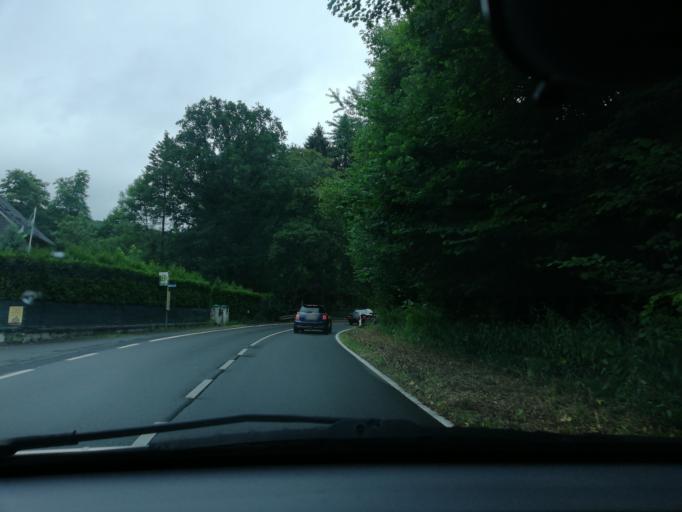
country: DE
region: North Rhine-Westphalia
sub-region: Regierungsbezirk Dusseldorf
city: Remscheid
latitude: 51.1930
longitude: 7.1494
